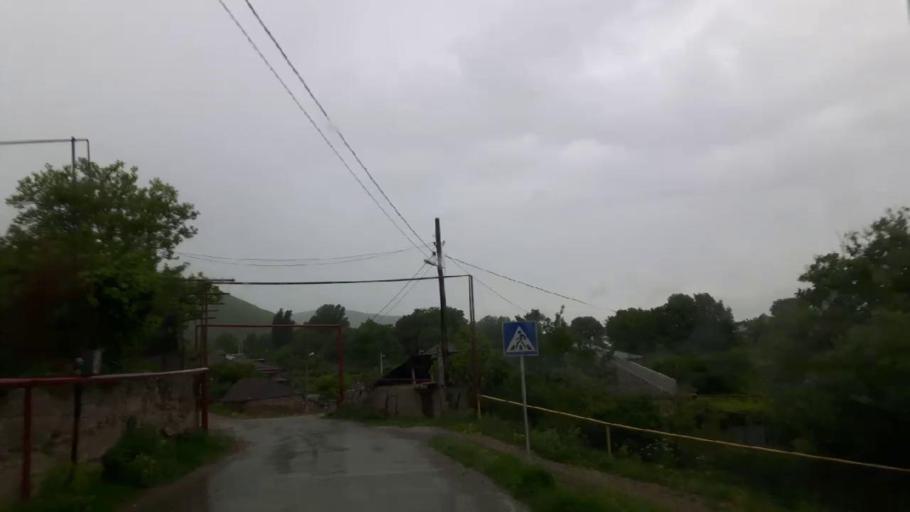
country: GE
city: Agara
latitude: 41.9848
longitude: 43.9233
